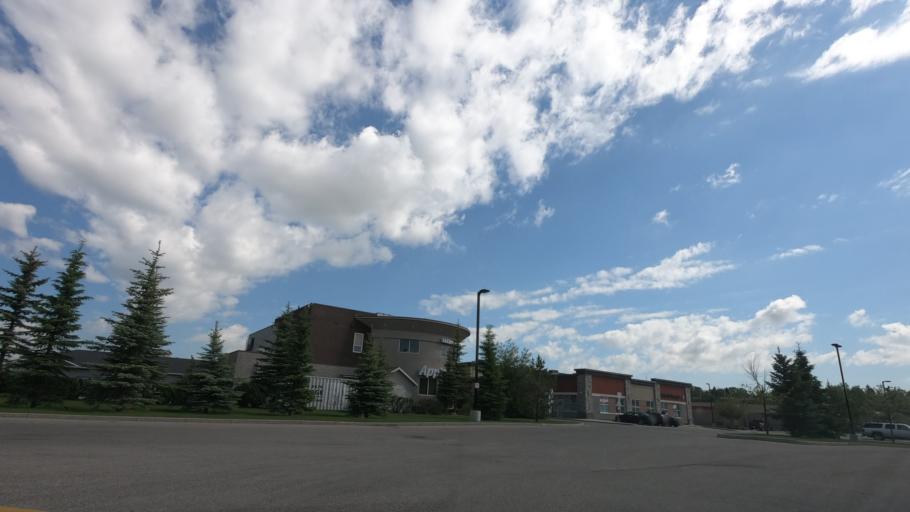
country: CA
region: Alberta
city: Airdrie
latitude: 51.2898
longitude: -114.0157
